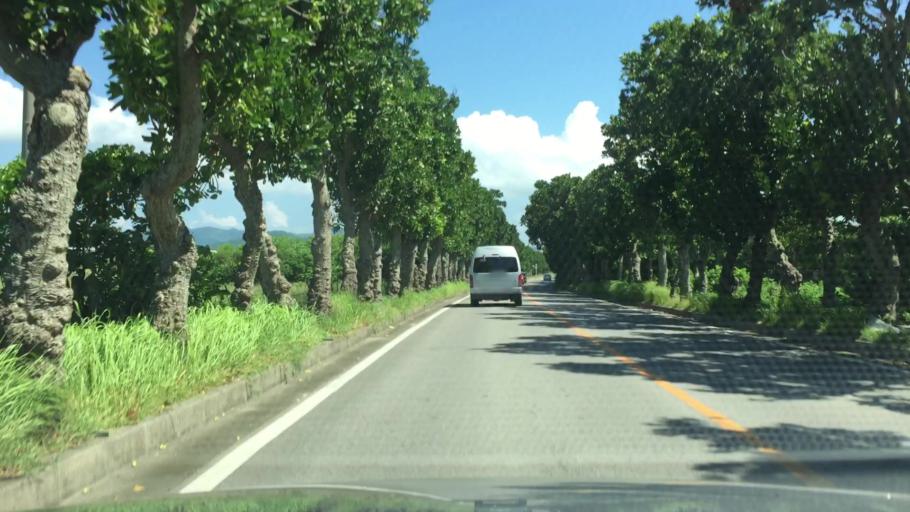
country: JP
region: Okinawa
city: Ishigaki
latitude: 24.3700
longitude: 124.2463
